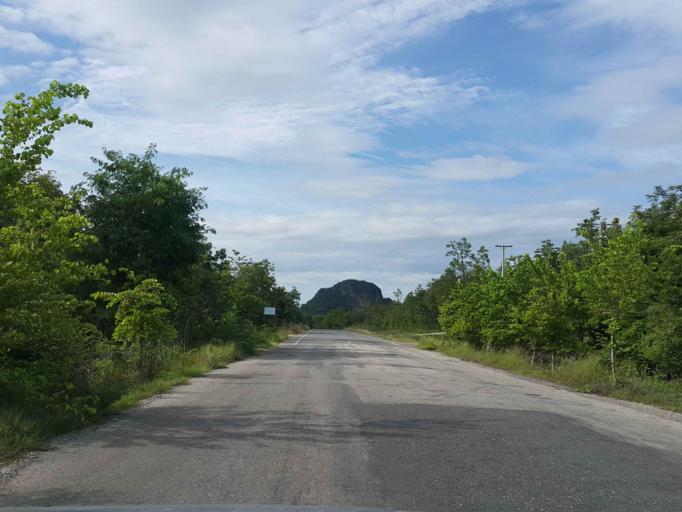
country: TH
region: Sukhothai
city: Thung Saliam
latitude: 17.2979
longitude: 99.5270
